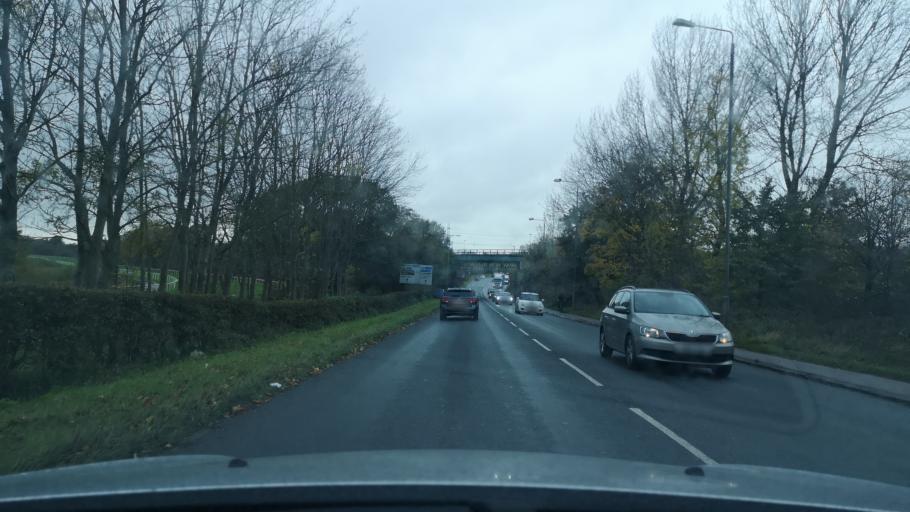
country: GB
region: England
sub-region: City and Borough of Wakefield
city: Pontefract
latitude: 53.7037
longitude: -1.3279
